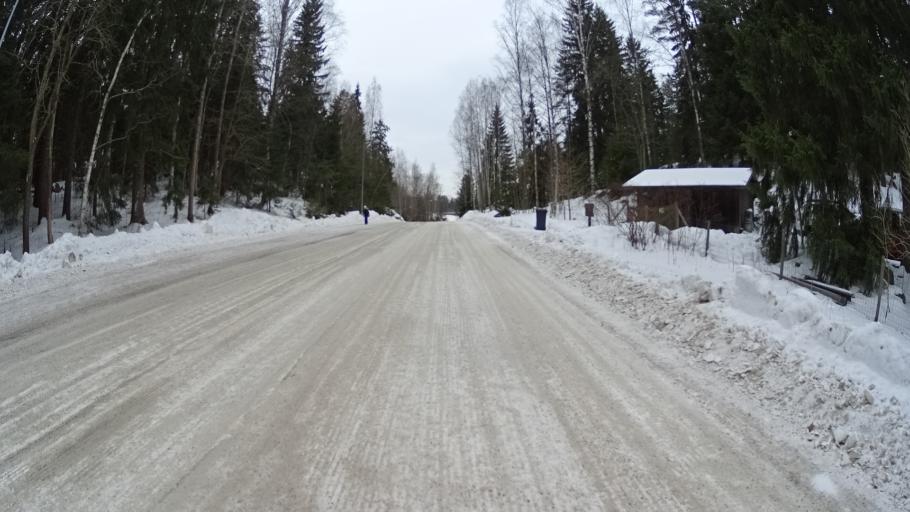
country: FI
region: Uusimaa
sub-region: Helsinki
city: Espoo
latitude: 60.2205
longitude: 24.6302
